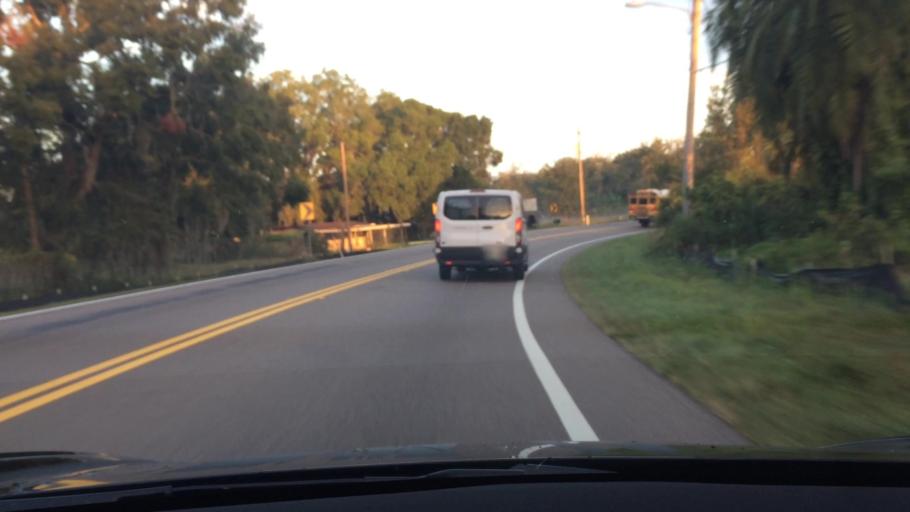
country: US
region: Florida
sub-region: Hillsborough County
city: Citrus Park
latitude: 28.0997
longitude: -82.5807
